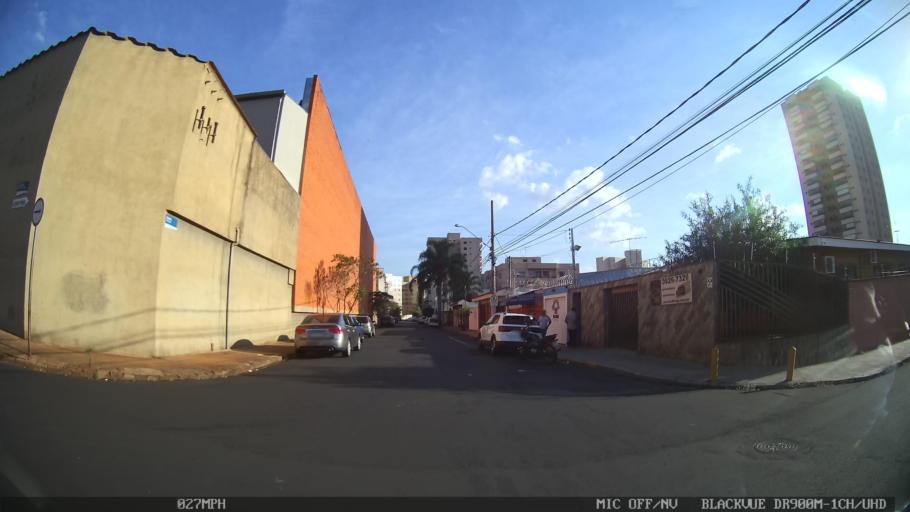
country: BR
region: Sao Paulo
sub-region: Ribeirao Preto
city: Ribeirao Preto
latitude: -21.1833
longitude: -47.7904
